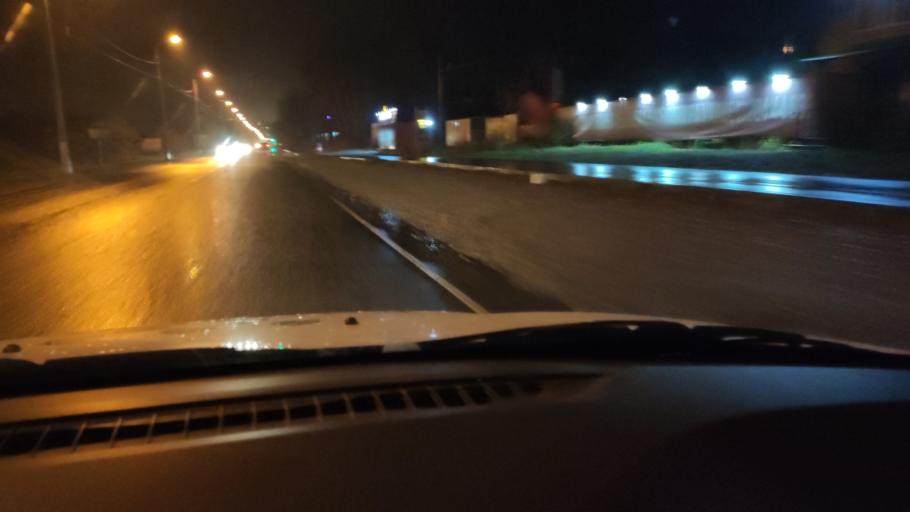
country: RU
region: Perm
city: Kondratovo
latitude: 57.9731
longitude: 56.1284
